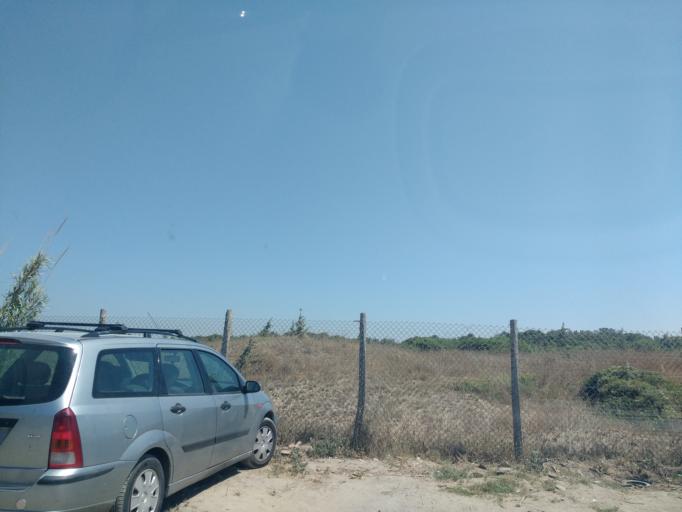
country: IT
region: Latium
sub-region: Citta metropolitana di Roma Capitale
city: Passo Oscuro
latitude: 41.8938
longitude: 12.1639
